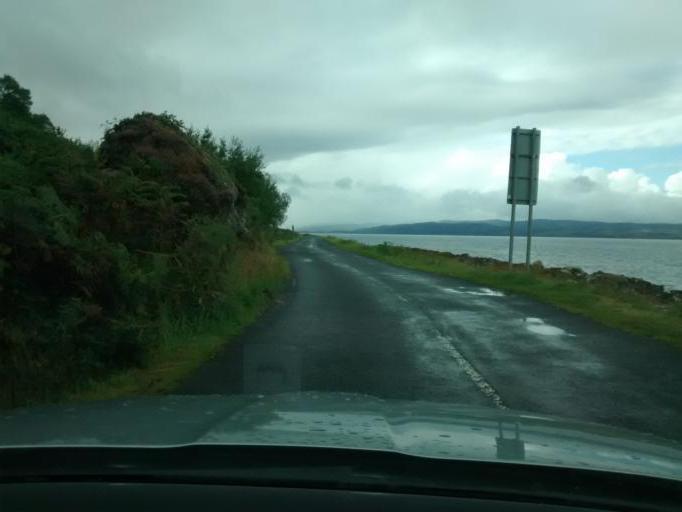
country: GB
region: Scotland
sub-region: North Ayrshire
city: Isle of Arran
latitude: 55.6743
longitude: -5.3688
